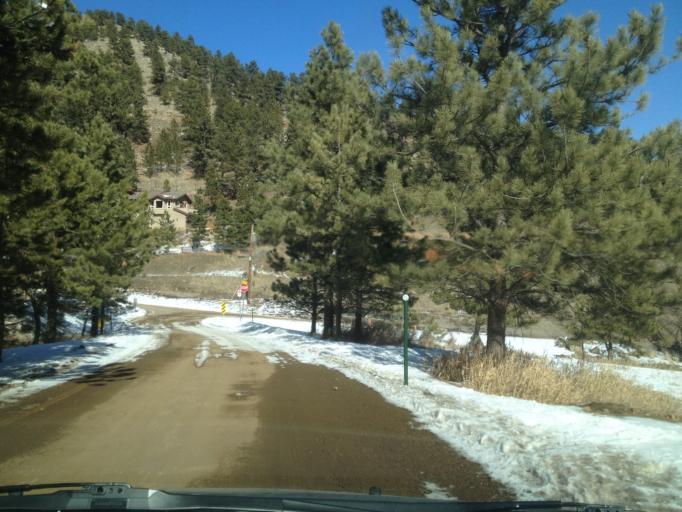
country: US
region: Colorado
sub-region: Boulder County
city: Boulder
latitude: 40.0604
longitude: -105.3184
